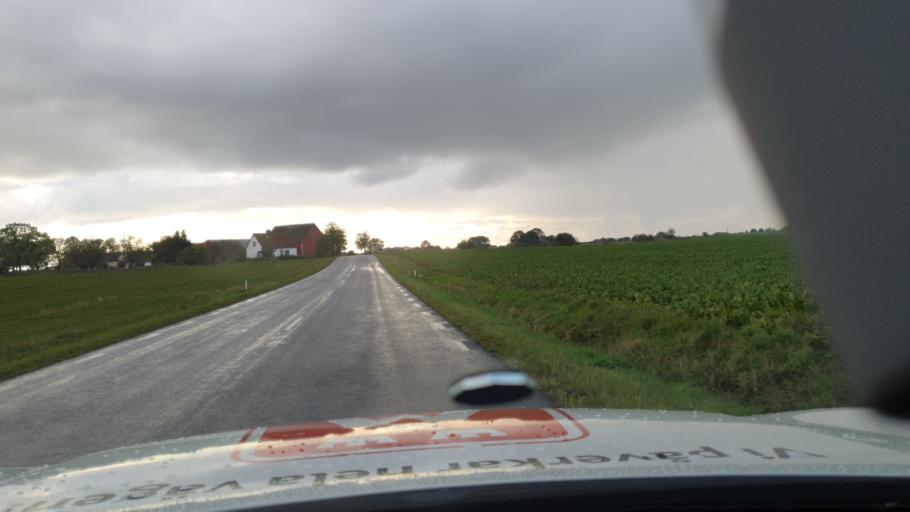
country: SE
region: Skane
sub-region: Trelleborgs Kommun
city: Anderslov
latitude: 55.4138
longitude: 13.2824
